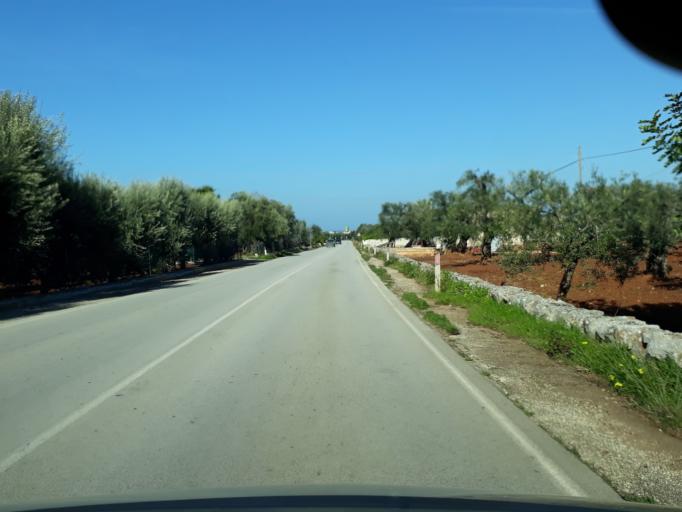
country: IT
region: Apulia
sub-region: Provincia di Bari
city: Monopoli
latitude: 40.9234
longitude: 17.2824
